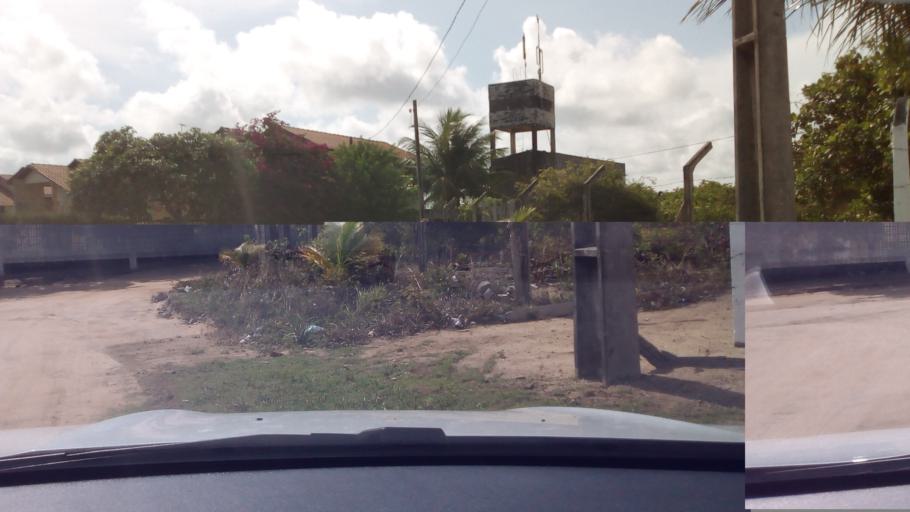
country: BR
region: Paraiba
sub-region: Conde
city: Conde
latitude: -7.3026
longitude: -34.8028
